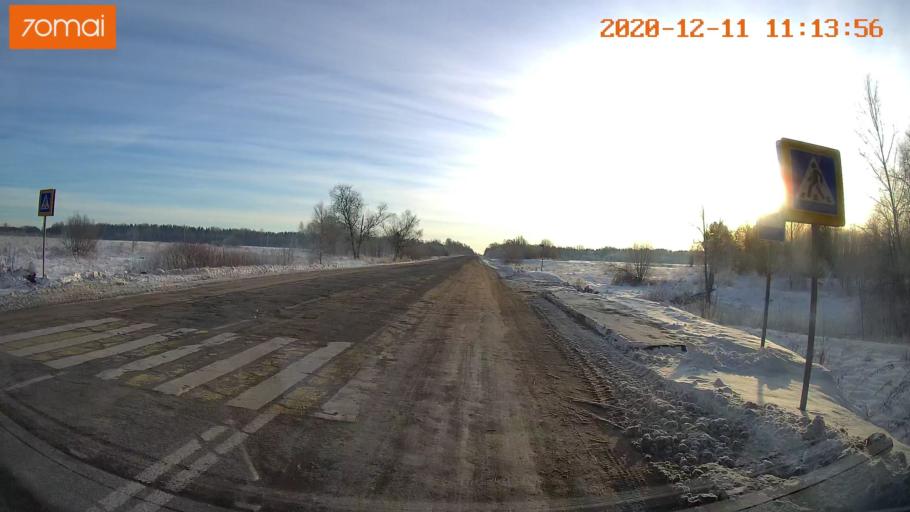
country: RU
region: Jaroslavl
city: Lyubim
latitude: 58.3263
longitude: 40.9144
